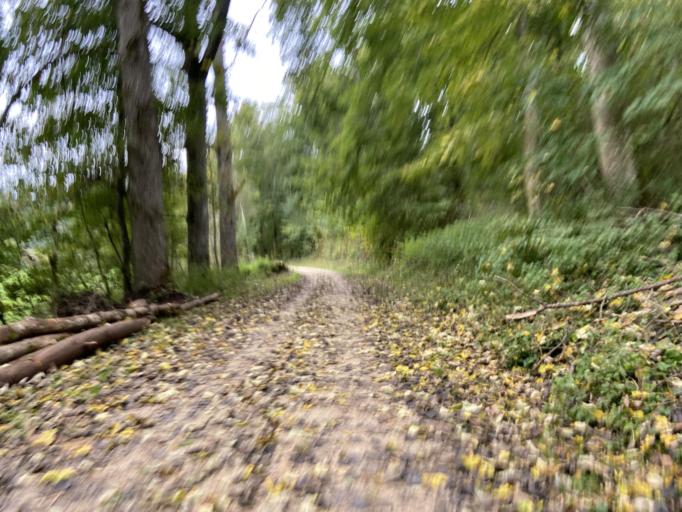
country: DE
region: Baden-Wuerttemberg
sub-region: Tuebingen Region
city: Sigmaringen
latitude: 48.1049
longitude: 9.2304
